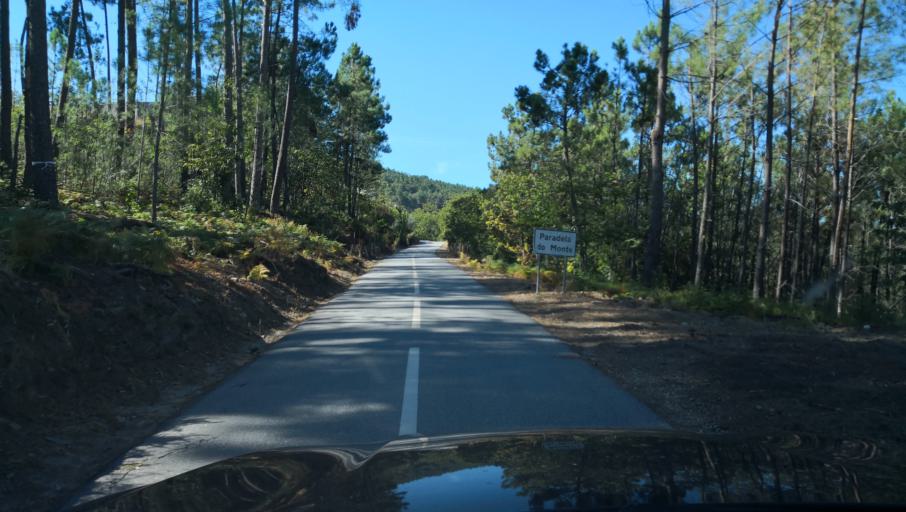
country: PT
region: Vila Real
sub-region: Santa Marta de Penaguiao
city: Santa Marta de Penaguiao
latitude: 41.2491
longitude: -7.8379
